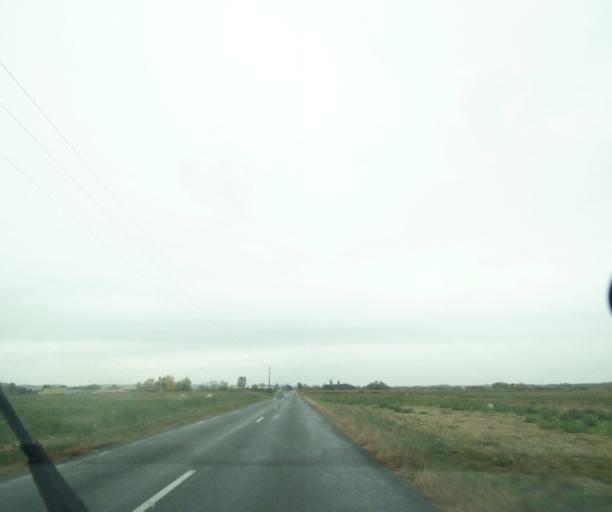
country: FR
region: Rhone-Alpes
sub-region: Departement de l'Ain
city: Saint-Maurice-de-Gourdans
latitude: 45.8021
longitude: 5.2124
